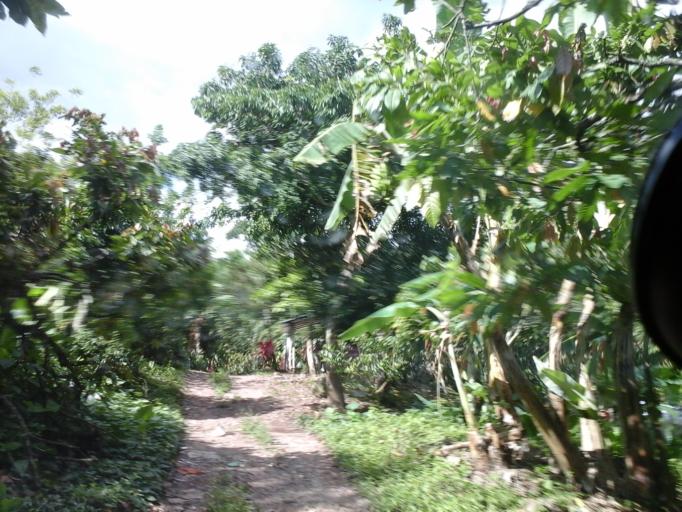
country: CO
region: Cesar
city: San Diego
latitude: 10.2846
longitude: -73.0876
